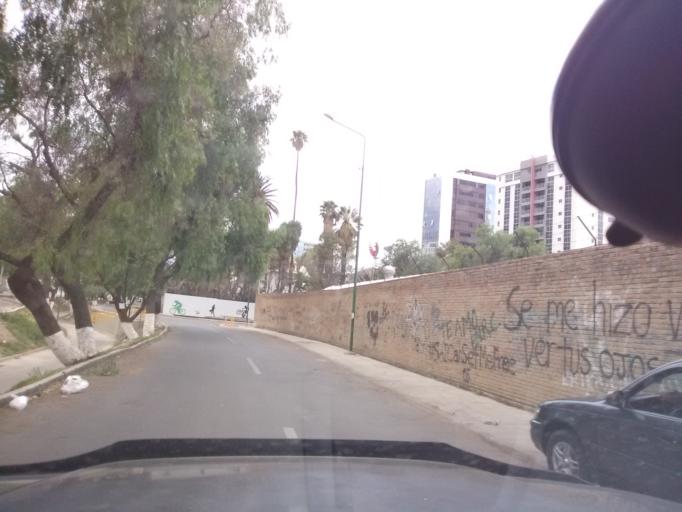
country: BO
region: Cochabamba
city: Cochabamba
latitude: -17.3726
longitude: -66.1482
